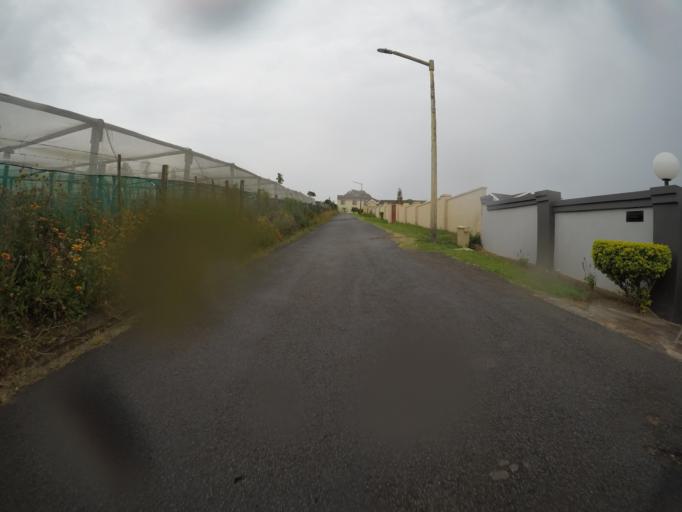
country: ZA
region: Eastern Cape
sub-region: Buffalo City Metropolitan Municipality
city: East London
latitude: -32.9869
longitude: 27.8592
